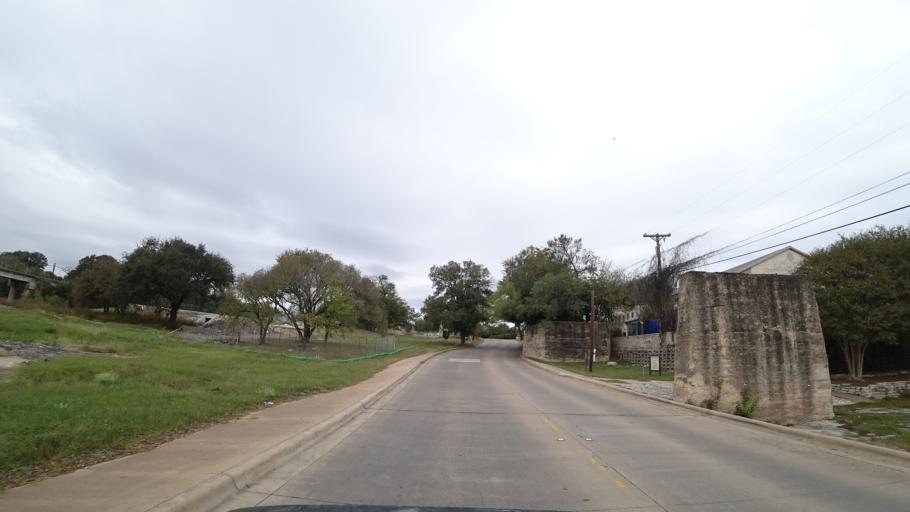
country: US
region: Texas
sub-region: Williamson County
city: Round Rock
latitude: 30.5132
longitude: -97.6895
